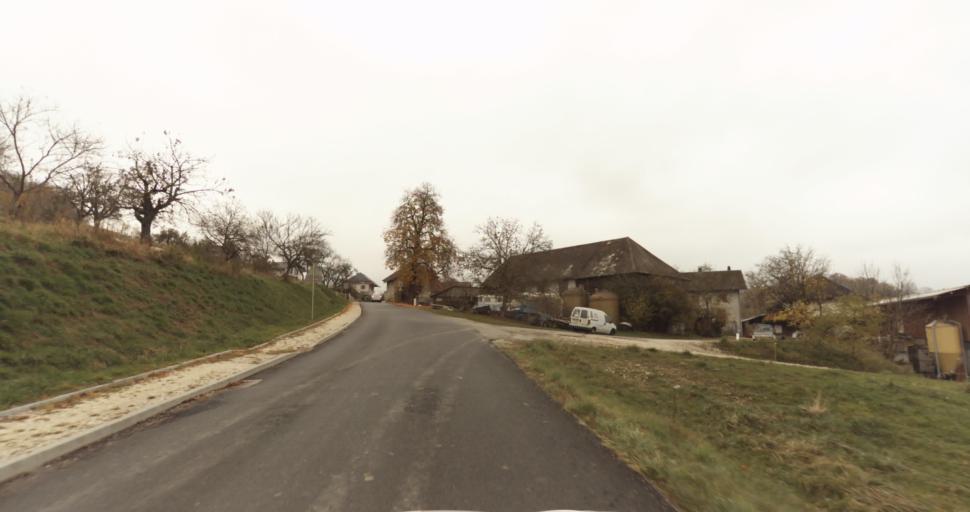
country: FR
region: Rhone-Alpes
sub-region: Departement de la Haute-Savoie
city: Saint-Felix
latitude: 45.7803
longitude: 5.9931
